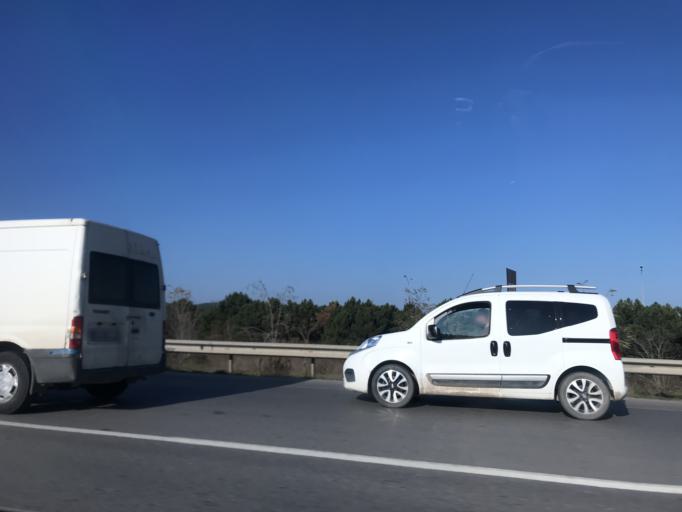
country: TR
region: Istanbul
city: Sultanbeyli
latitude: 40.9326
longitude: 29.3377
